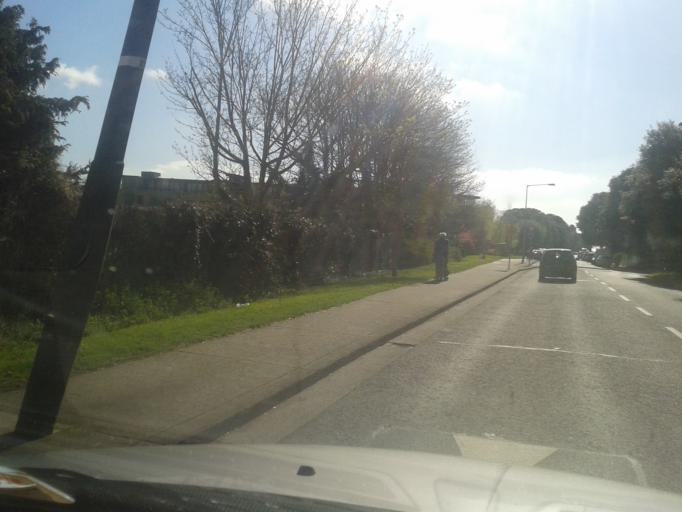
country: IE
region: Leinster
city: Raheny
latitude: 53.3777
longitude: -6.1721
